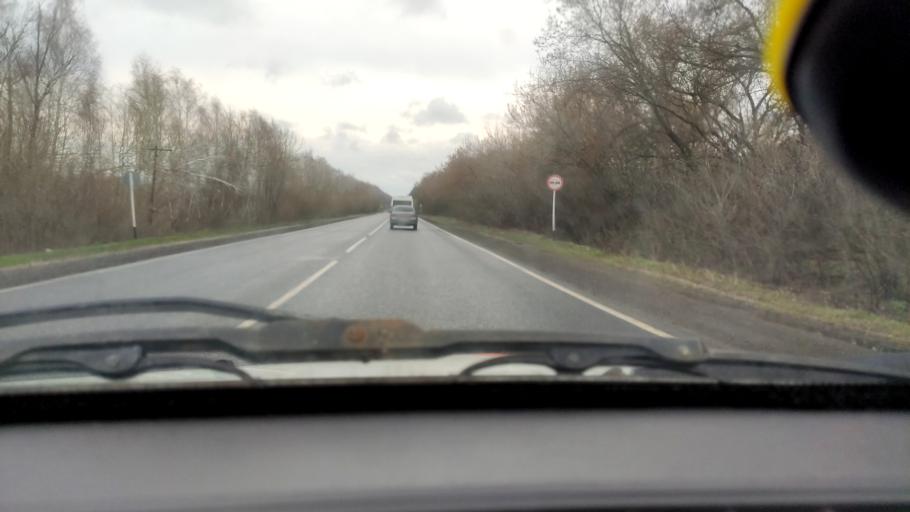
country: RU
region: Samara
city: Povolzhskiy
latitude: 53.6069
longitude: 49.6089
